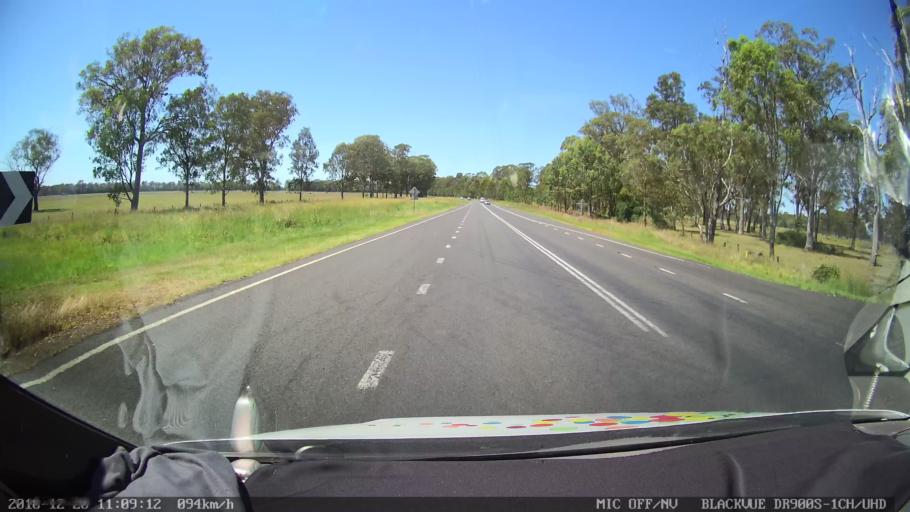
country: AU
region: New South Wales
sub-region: Richmond Valley
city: Casino
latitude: -28.9329
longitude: 153.0049
